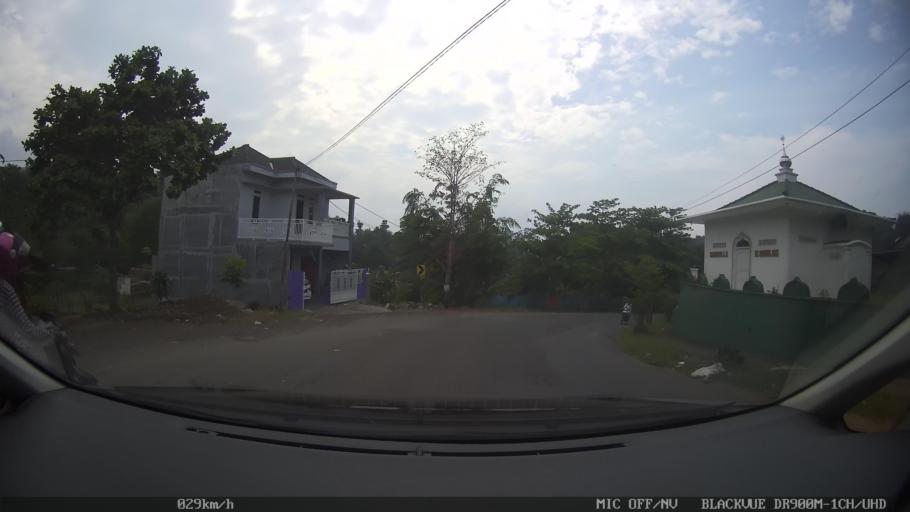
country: ID
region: Lampung
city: Bandarlampung
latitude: -5.4357
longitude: 105.2431
